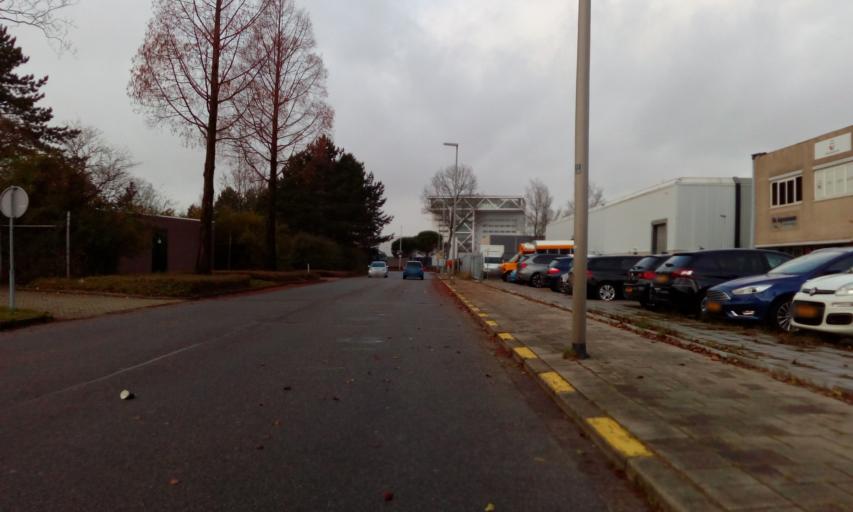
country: NL
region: South Holland
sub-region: Gemeente Zoetermeer
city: Zoetermeer
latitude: 52.0413
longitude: 4.5118
